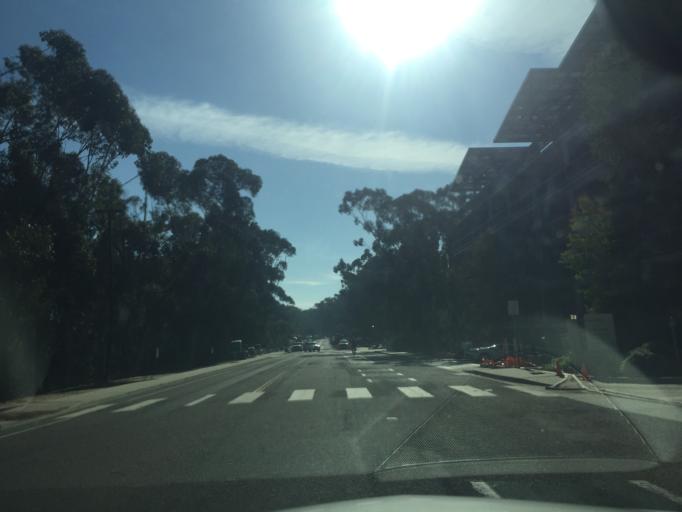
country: US
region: California
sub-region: San Diego County
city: La Jolla
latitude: 32.8843
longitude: -117.2386
